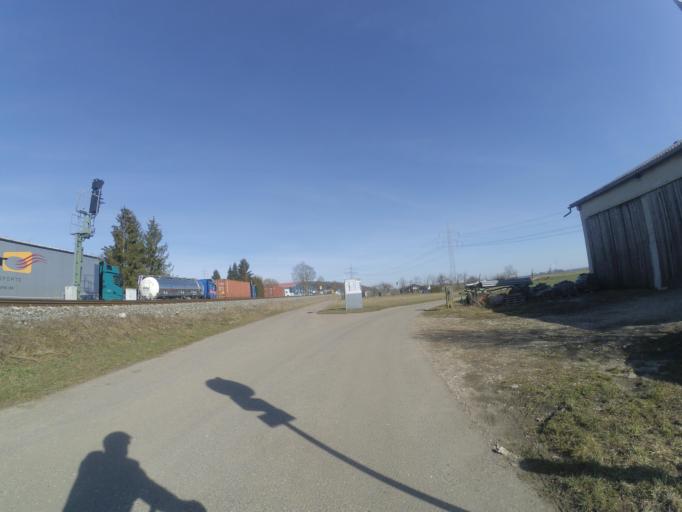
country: DE
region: Baden-Wuerttemberg
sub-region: Regierungsbezirk Stuttgart
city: Niederstotzingen
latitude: 48.5362
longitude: 10.2426
